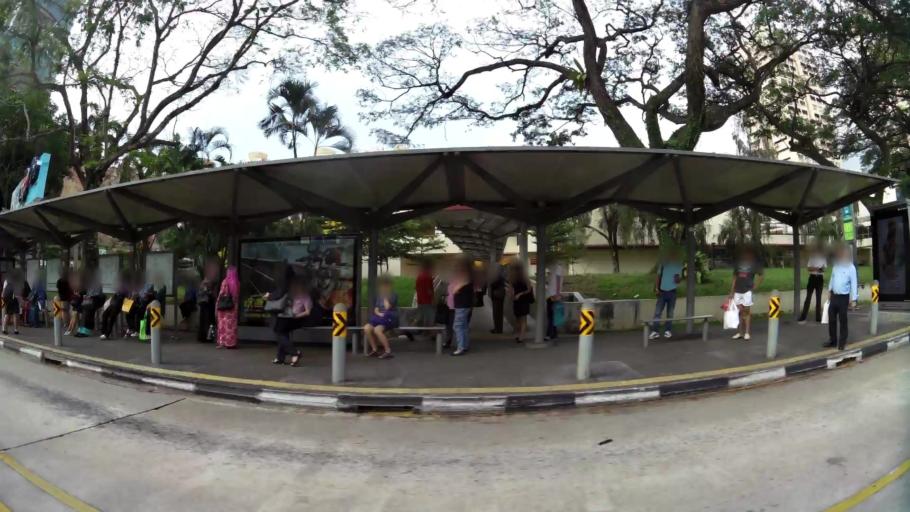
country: SG
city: Singapore
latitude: 1.3312
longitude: 103.8503
